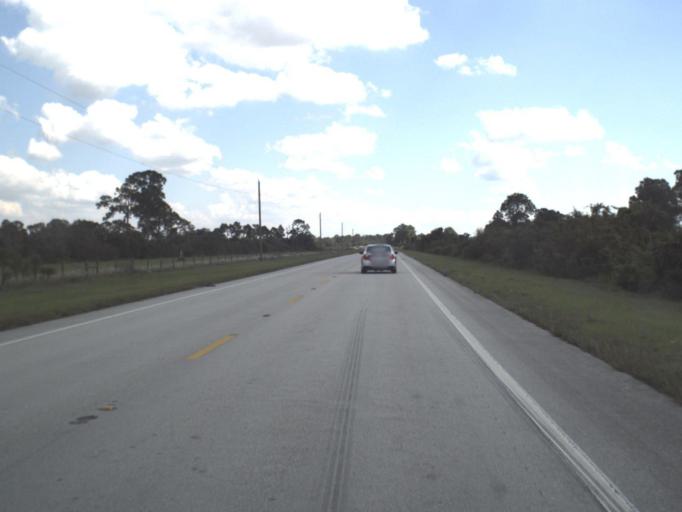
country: US
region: Florida
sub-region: Highlands County
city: Lake Placid
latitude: 27.3862
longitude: -81.1366
